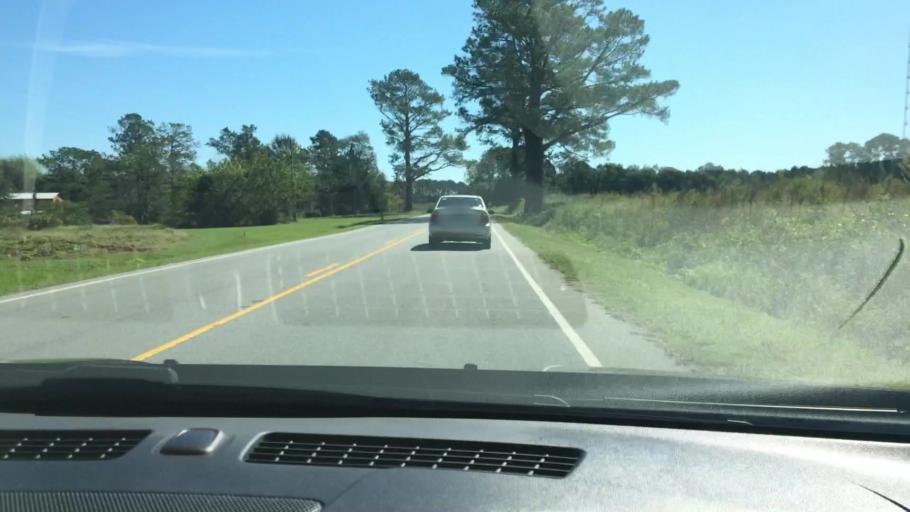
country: US
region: North Carolina
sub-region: Pitt County
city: Grifton
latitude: 35.3449
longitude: -77.3193
